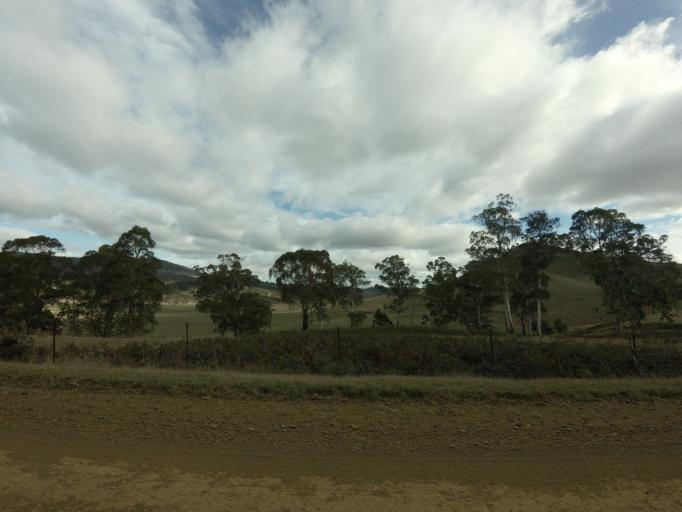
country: AU
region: Tasmania
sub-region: Brighton
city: Bridgewater
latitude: -42.4819
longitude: 147.2971
